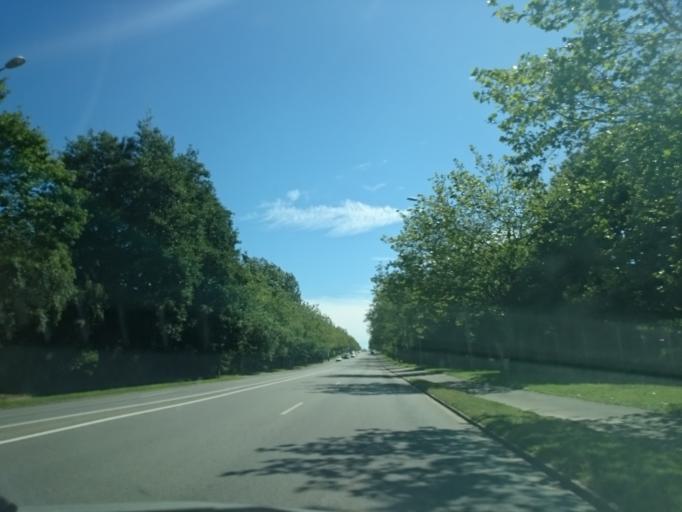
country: FR
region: Brittany
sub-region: Departement du Finistere
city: Bohars
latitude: 48.4127
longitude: -4.5068
